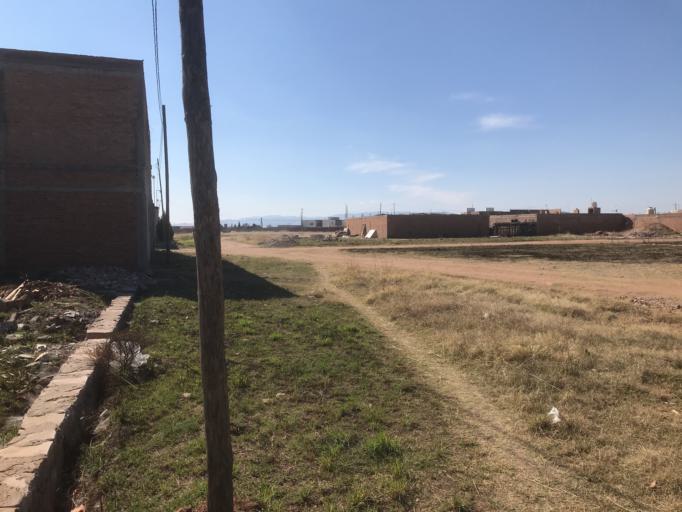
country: MX
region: Durango
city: Victoria de Durango
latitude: 24.0246
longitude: -104.5897
